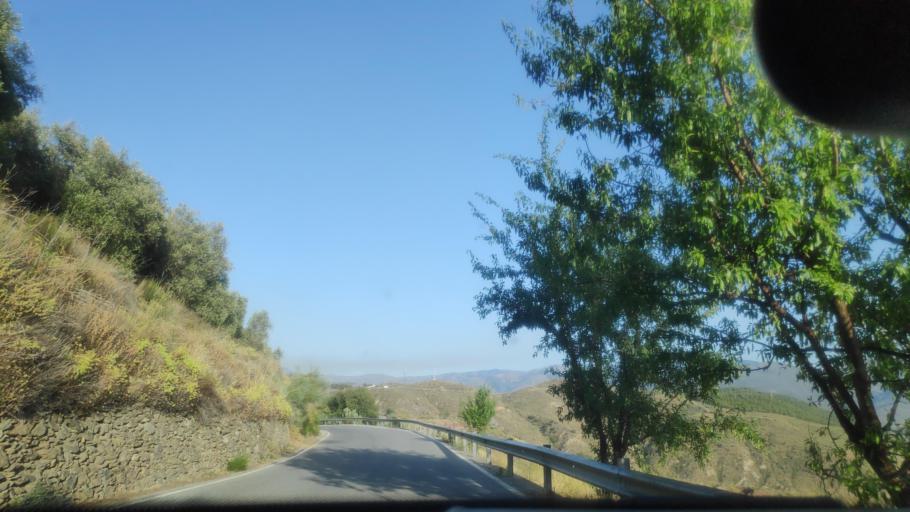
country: ES
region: Andalusia
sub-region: Provincia de Granada
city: Soportujar
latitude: 36.9267
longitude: -3.4017
